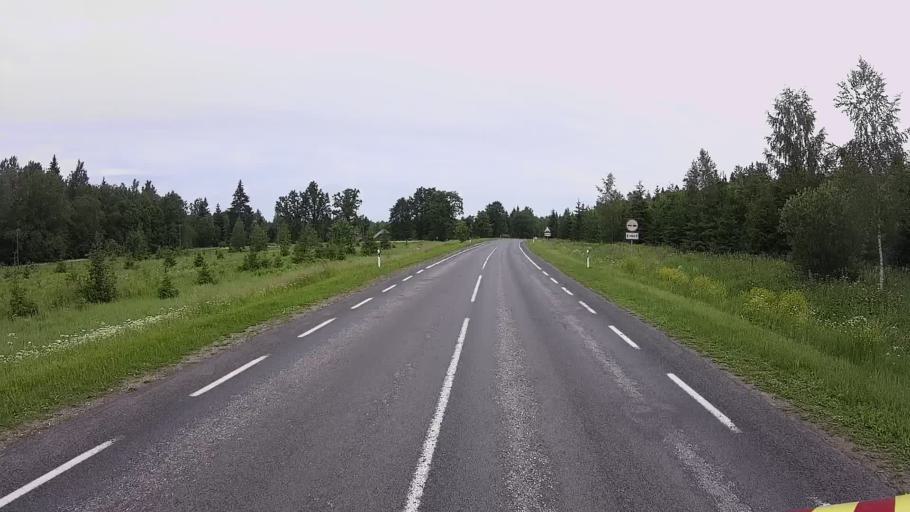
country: EE
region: Viljandimaa
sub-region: Karksi vald
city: Karksi-Nuia
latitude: 58.1818
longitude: 25.5927
